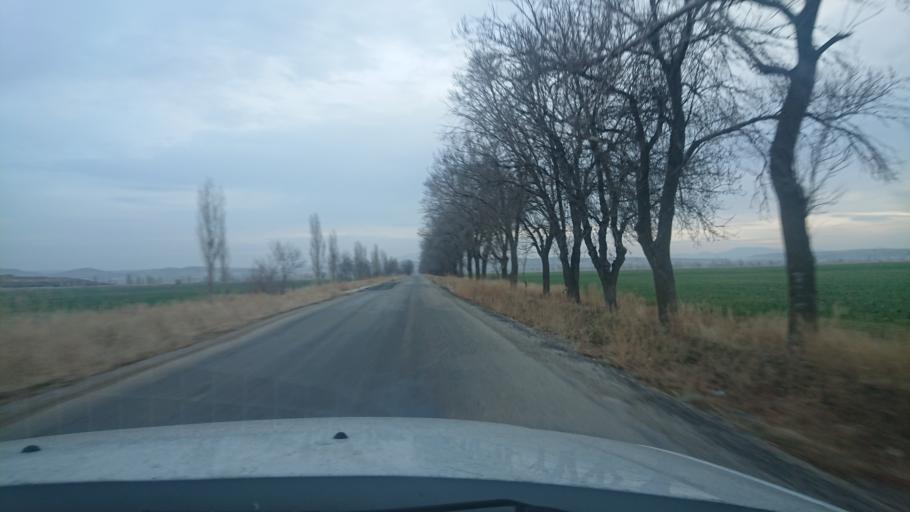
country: TR
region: Aksaray
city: Yesilova
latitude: 38.4639
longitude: 33.8434
